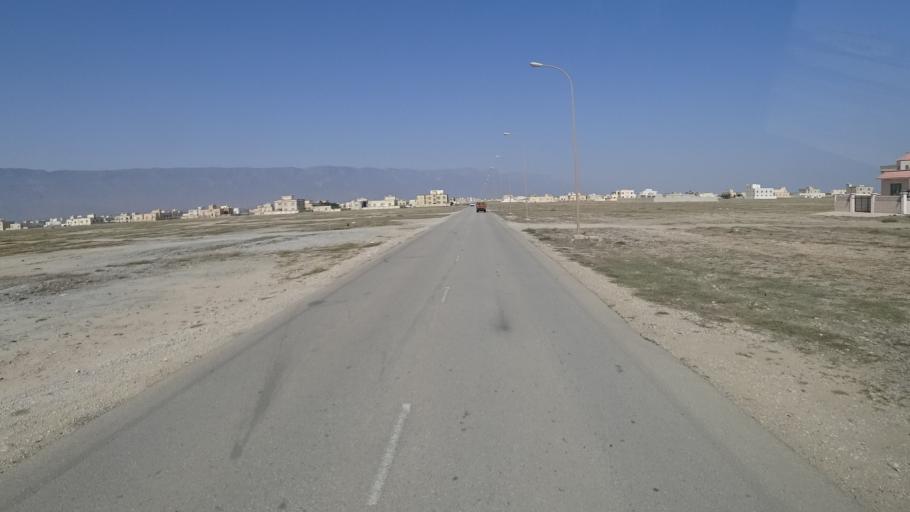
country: OM
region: Zufar
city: Salalah
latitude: 16.9830
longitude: 54.7114
